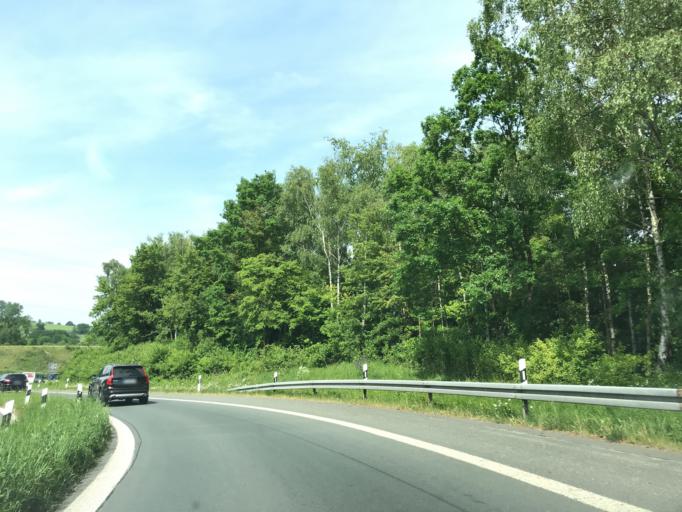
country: DE
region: North Rhine-Westphalia
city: Witten
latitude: 51.4351
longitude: 7.2907
